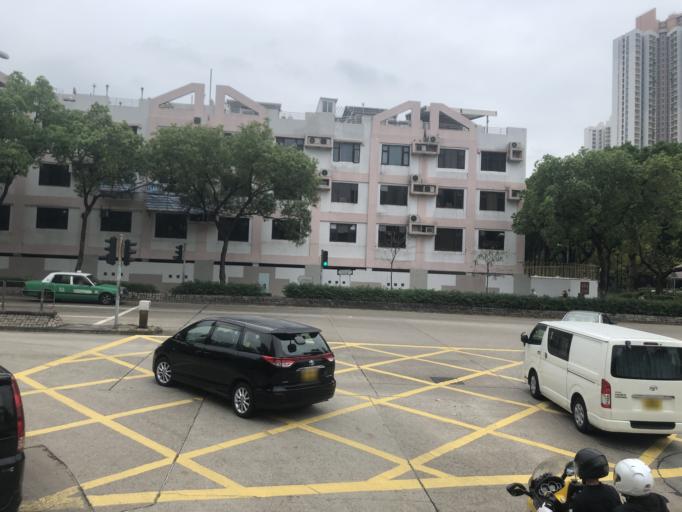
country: HK
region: Tai Po
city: Tai Po
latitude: 22.4958
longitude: 114.1300
